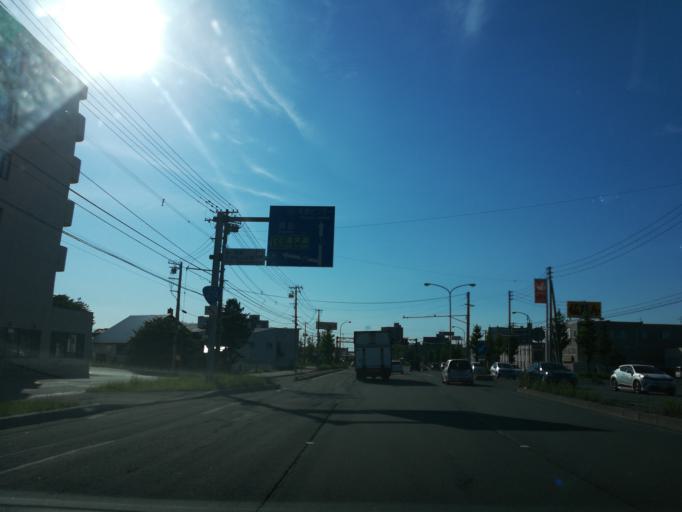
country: JP
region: Hokkaido
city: Kitahiroshima
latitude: 43.0238
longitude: 141.4680
